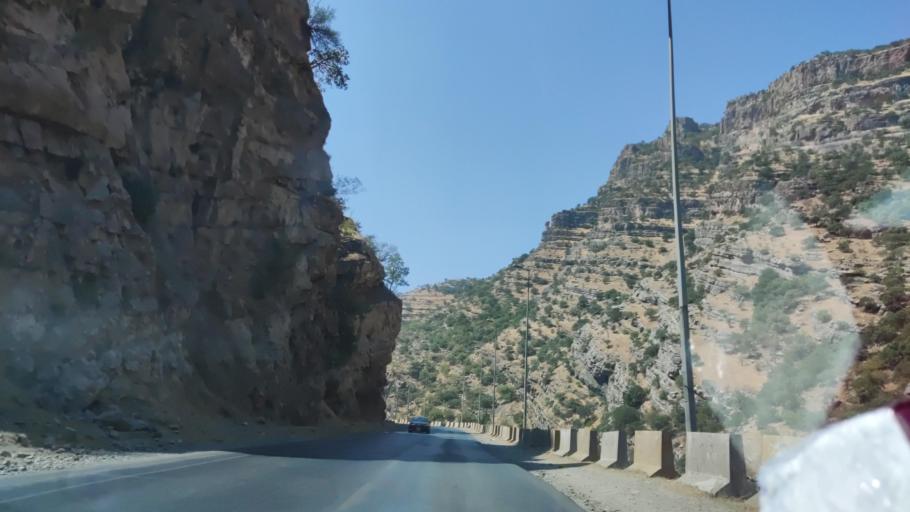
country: IQ
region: Arbil
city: Ruwandiz
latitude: 36.6435
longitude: 44.4943
